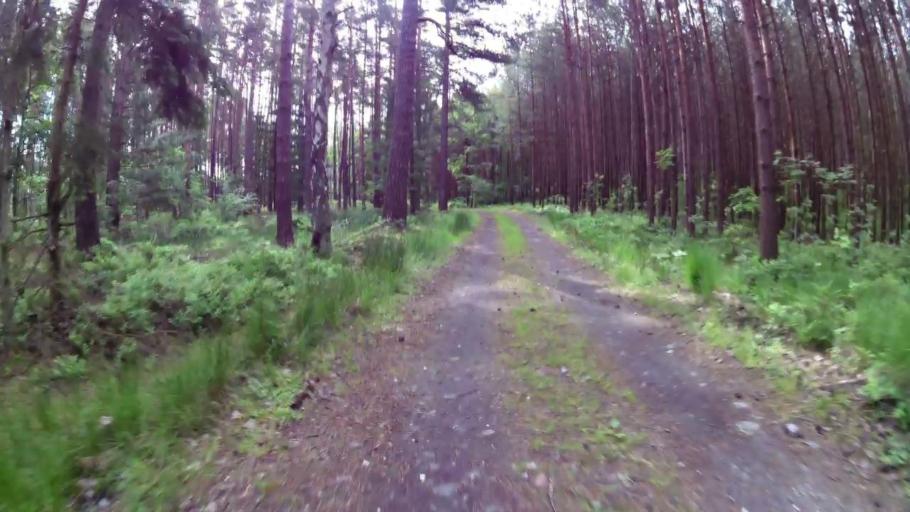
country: PL
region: West Pomeranian Voivodeship
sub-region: Swinoujscie
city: Swinoujscie
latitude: 53.9097
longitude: 14.3129
